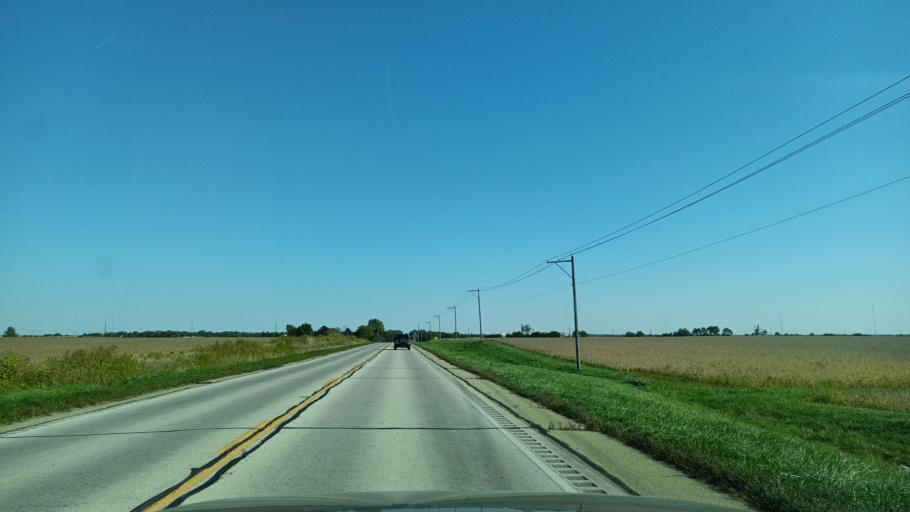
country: US
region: Illinois
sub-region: Champaign County
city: Lake of the Woods
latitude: 40.1760
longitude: -88.3475
